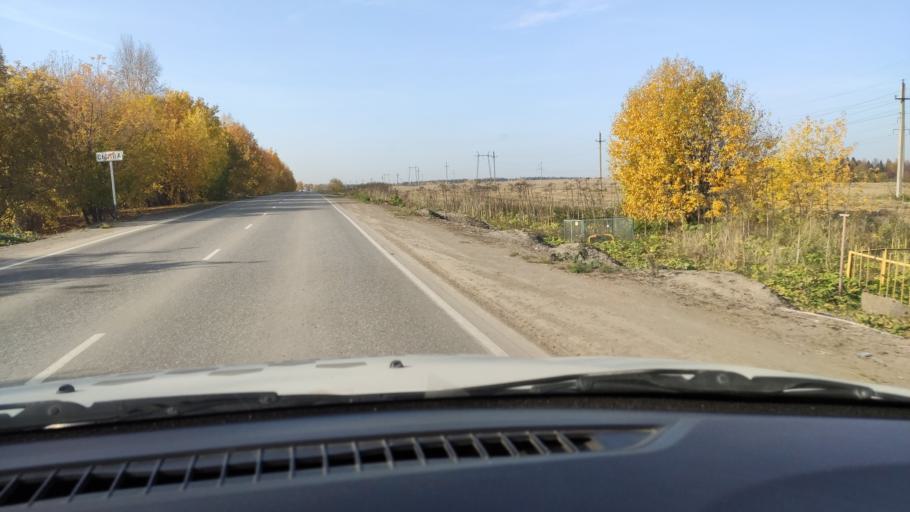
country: RU
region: Perm
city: Sylva
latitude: 58.0289
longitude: 56.7041
